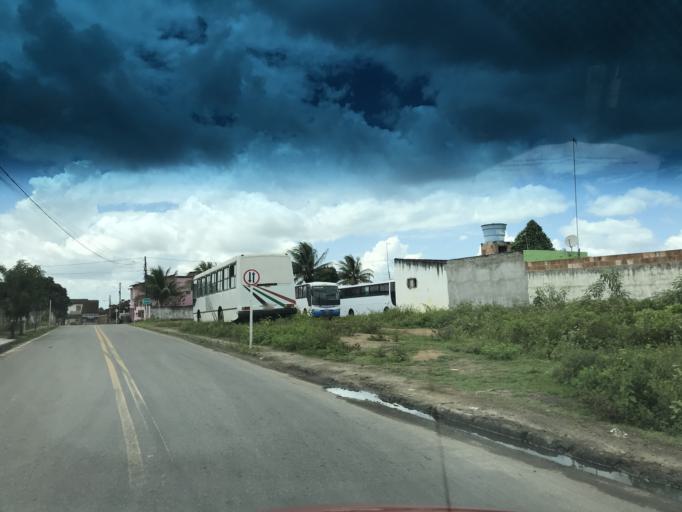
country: BR
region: Bahia
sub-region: Conceicao Do Almeida
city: Conceicao do Almeida
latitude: -12.7371
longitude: -39.1864
